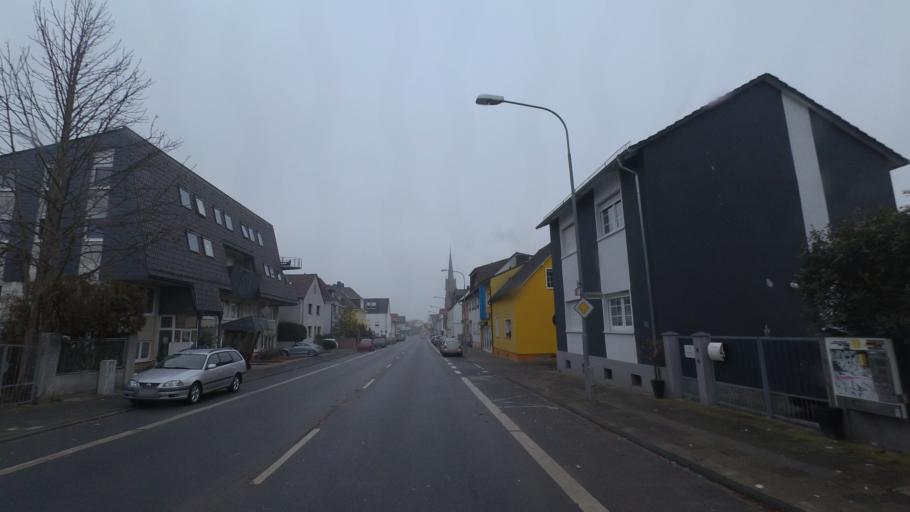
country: DE
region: Hesse
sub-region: Regierungsbezirk Darmstadt
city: Seligenstadt
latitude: 50.0549
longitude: 8.9308
